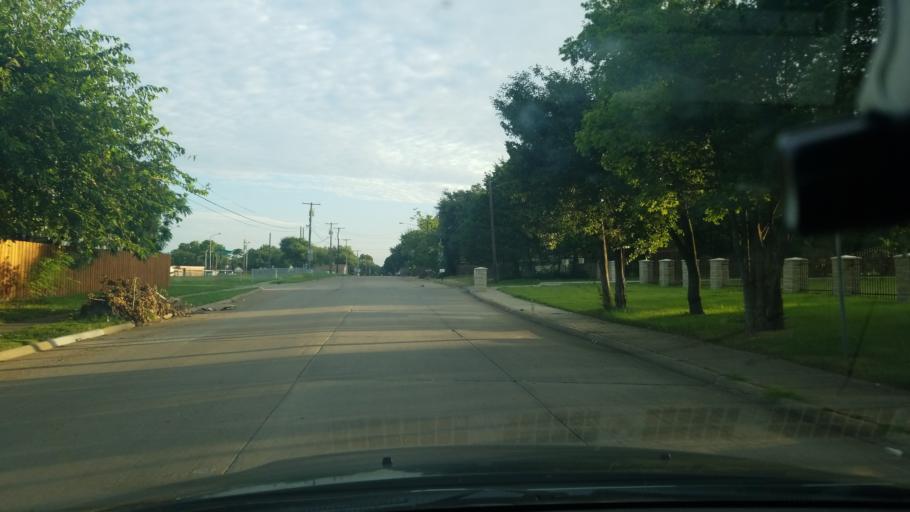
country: US
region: Texas
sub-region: Dallas County
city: Balch Springs
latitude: 32.7388
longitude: -96.6398
